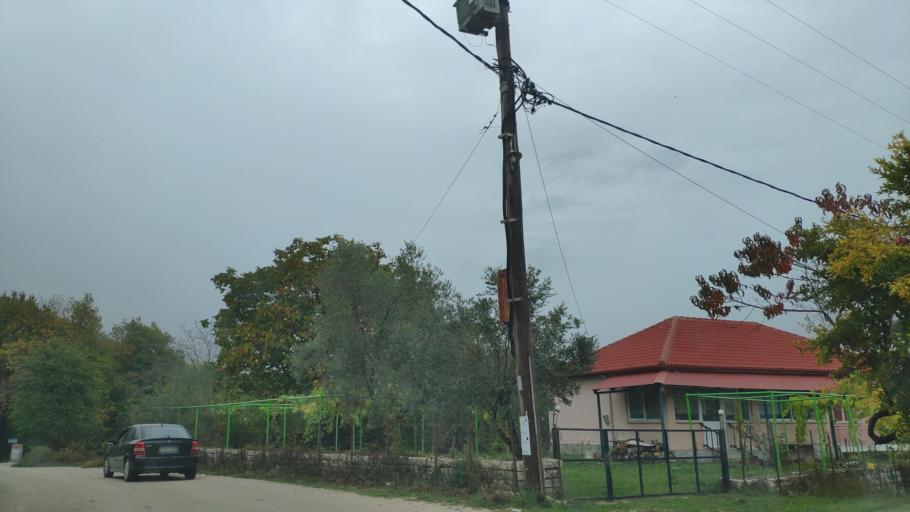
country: GR
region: Epirus
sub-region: Nomos Thesprotias
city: Paramythia
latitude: 39.4715
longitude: 20.6694
